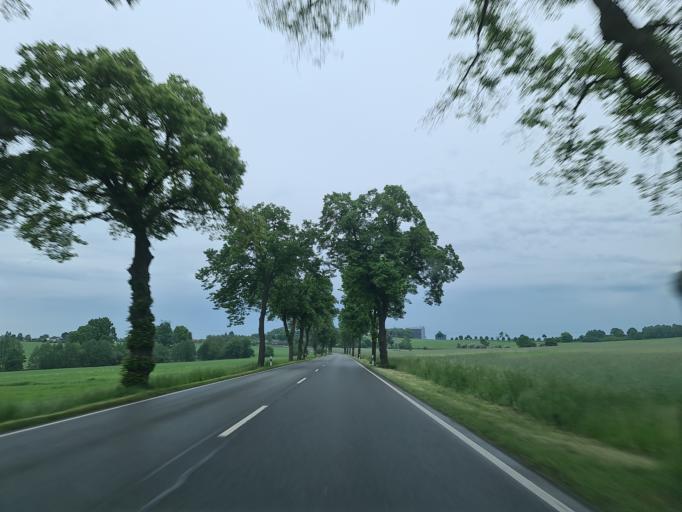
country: DE
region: Saxony
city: Oelsnitz
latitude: 50.4486
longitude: 12.1609
